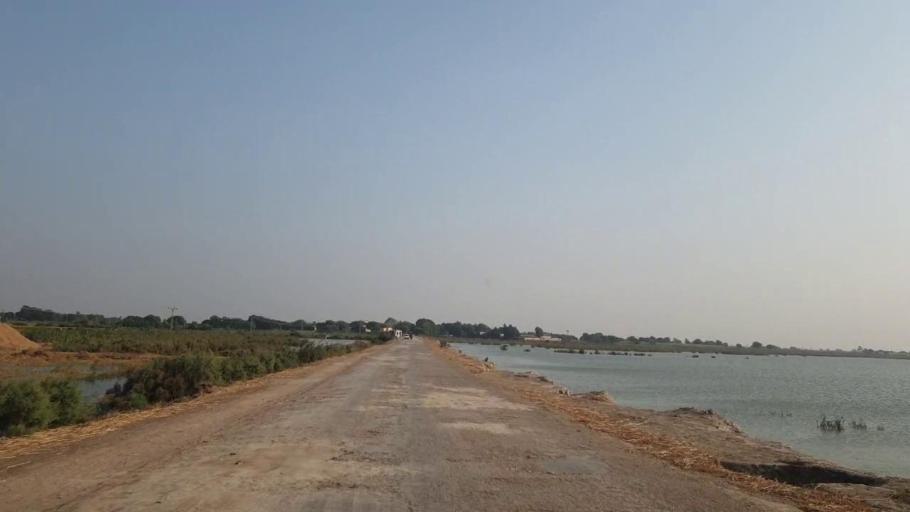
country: PK
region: Sindh
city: Bulri
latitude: 24.9904
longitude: 68.3878
